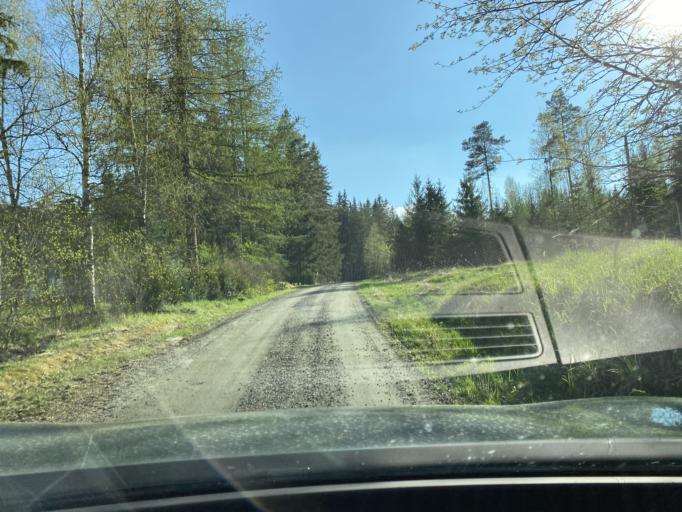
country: FI
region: Pirkanmaa
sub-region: Lounais-Pirkanmaa
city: Punkalaidun
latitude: 61.0293
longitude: 23.2186
